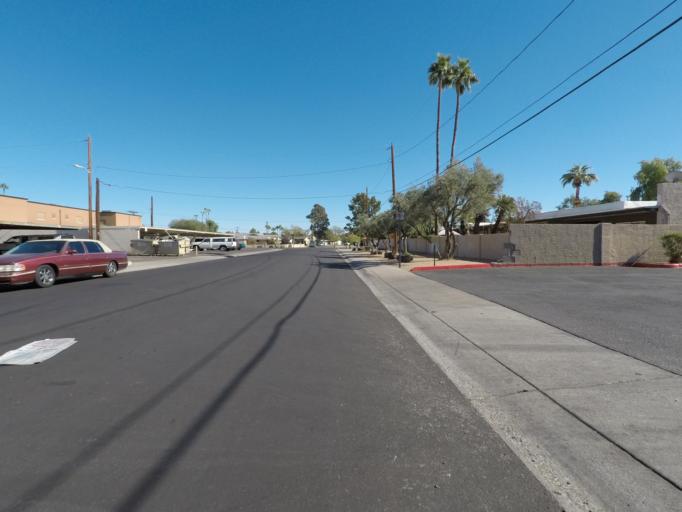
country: US
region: Arizona
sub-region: Maricopa County
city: Phoenix
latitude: 33.5158
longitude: -112.0921
